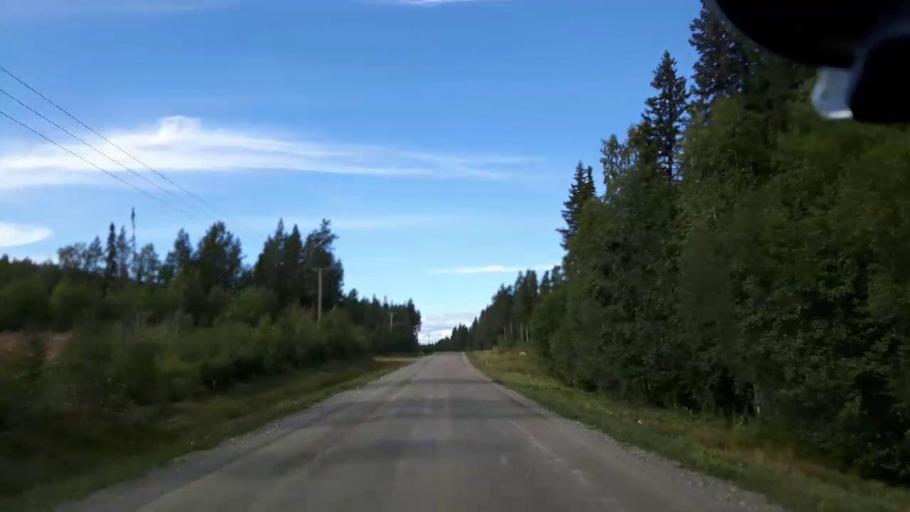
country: SE
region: Jaemtland
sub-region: Ragunda Kommun
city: Hammarstrand
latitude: 63.1403
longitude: 16.2318
